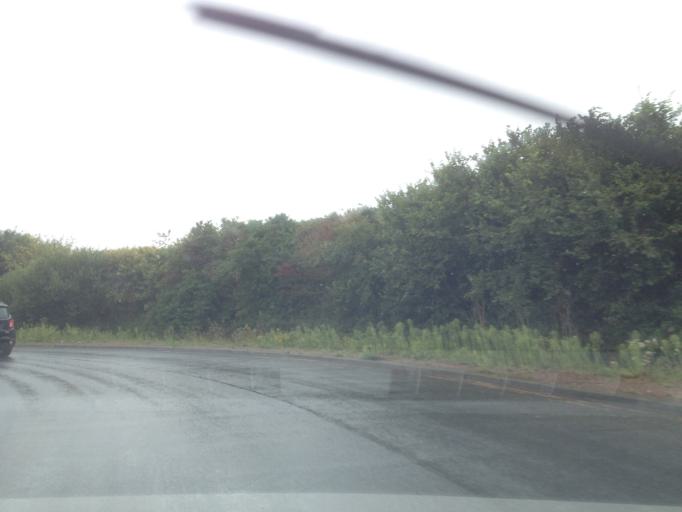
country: FR
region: Lower Normandy
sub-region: Departement du Calvados
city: Port-en-Bessin-Huppain
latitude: 49.2900
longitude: -0.7571
